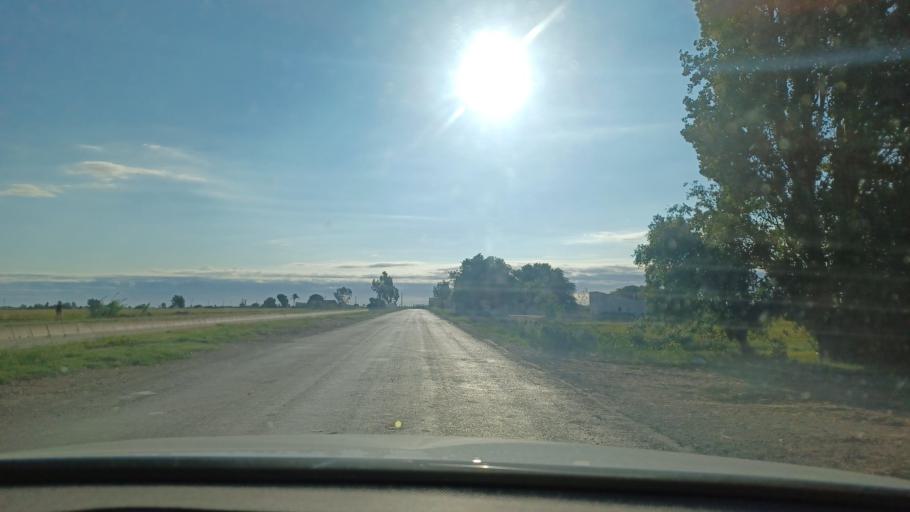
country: ES
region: Catalonia
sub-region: Provincia de Tarragona
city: Amposta
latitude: 40.6995
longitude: 0.6103
